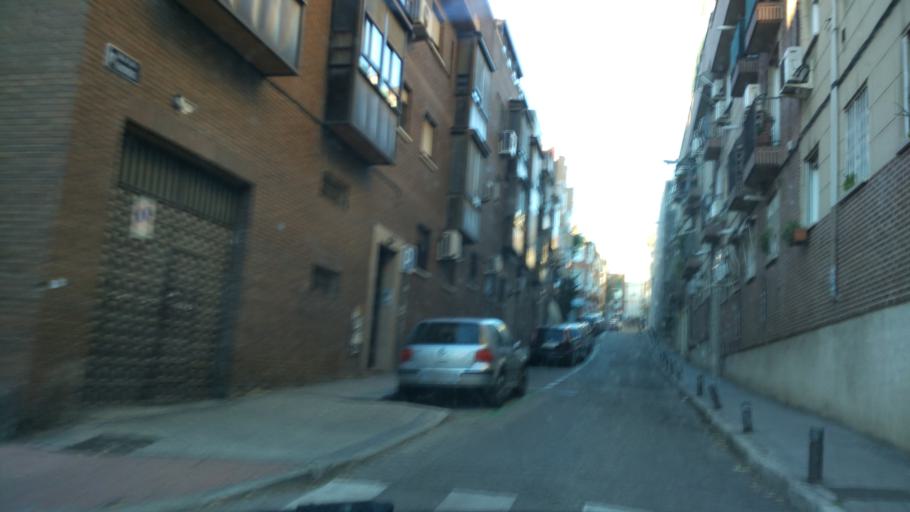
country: ES
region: Madrid
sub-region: Provincia de Madrid
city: Tetuan de las Victorias
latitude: 40.4650
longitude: -3.7050
